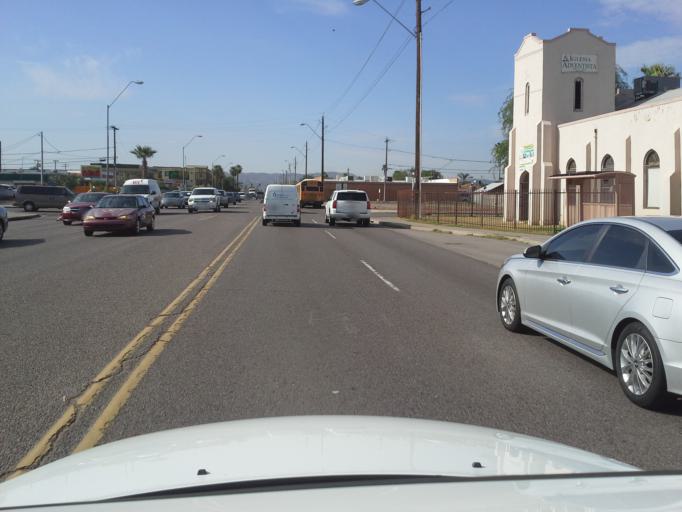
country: US
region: Arizona
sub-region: Maricopa County
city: Phoenix
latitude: 33.4577
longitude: -112.0477
